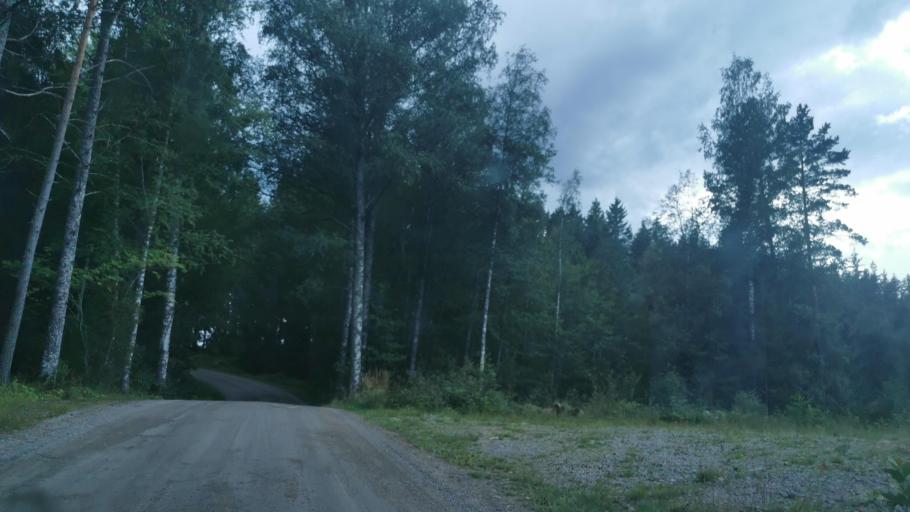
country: SE
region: OEstergoetland
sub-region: Finspangs Kommun
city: Finspang
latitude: 58.7897
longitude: 15.7675
